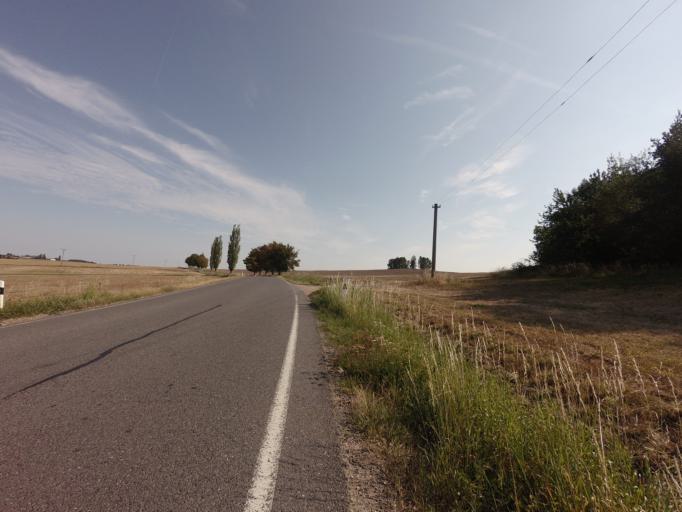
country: CZ
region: Jihocesky
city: Bernartice
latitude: 49.3280
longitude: 14.3593
